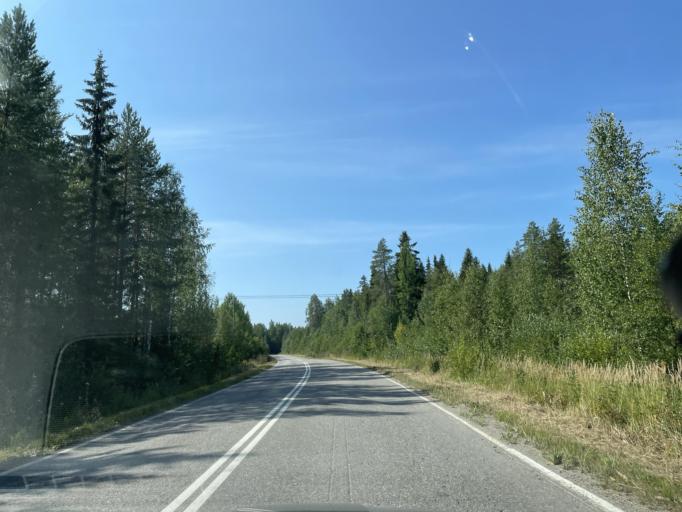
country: FI
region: Central Finland
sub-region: Saarijaervi-Viitasaari
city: Pihtipudas
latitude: 63.3640
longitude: 25.7295
